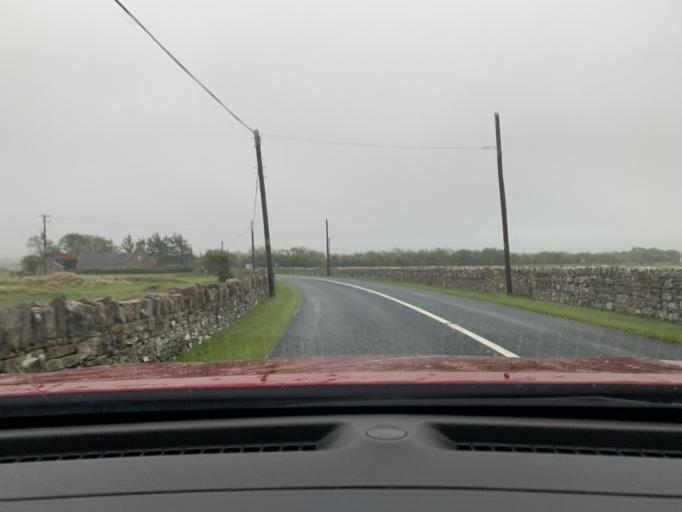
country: IE
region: Connaught
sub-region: County Leitrim
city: Kinlough
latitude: 54.4529
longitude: -8.4536
